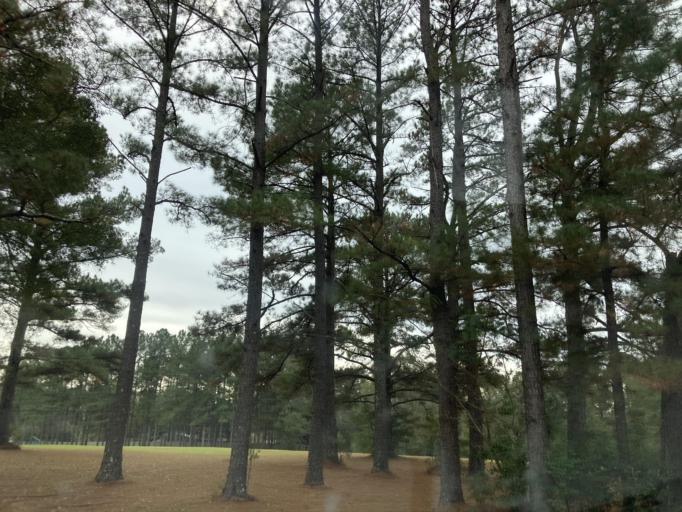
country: US
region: Mississippi
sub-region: Lamar County
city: Lumberton
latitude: 31.0573
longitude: -89.4784
